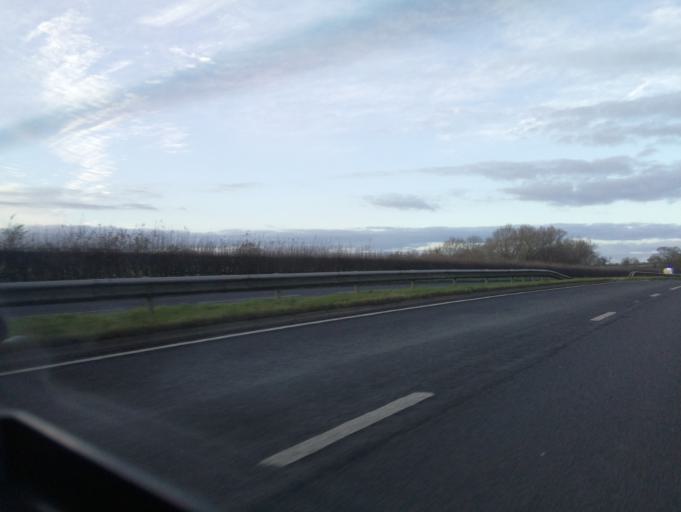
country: GB
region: England
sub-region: Staffordshire
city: Stafford
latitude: 52.8437
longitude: -2.1371
